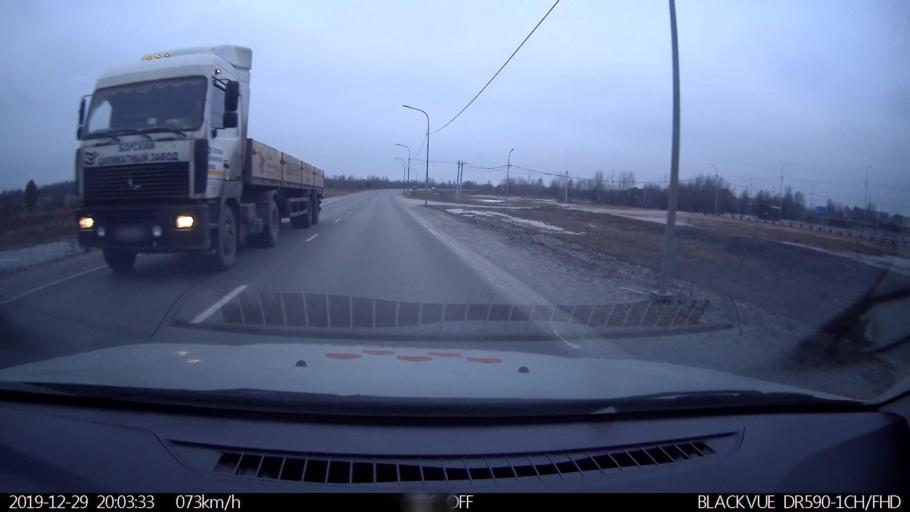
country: RU
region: Nizjnij Novgorod
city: Nizhniy Novgorod
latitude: 56.3748
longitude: 44.0162
